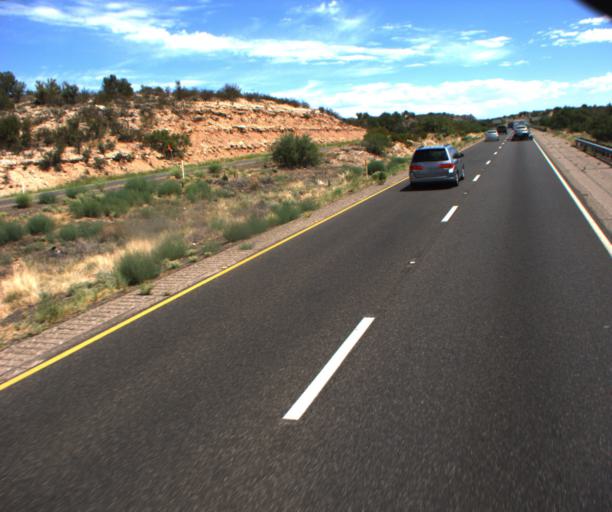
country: US
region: Arizona
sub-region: Yavapai County
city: Lake Montezuma
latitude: 34.6497
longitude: -111.8001
